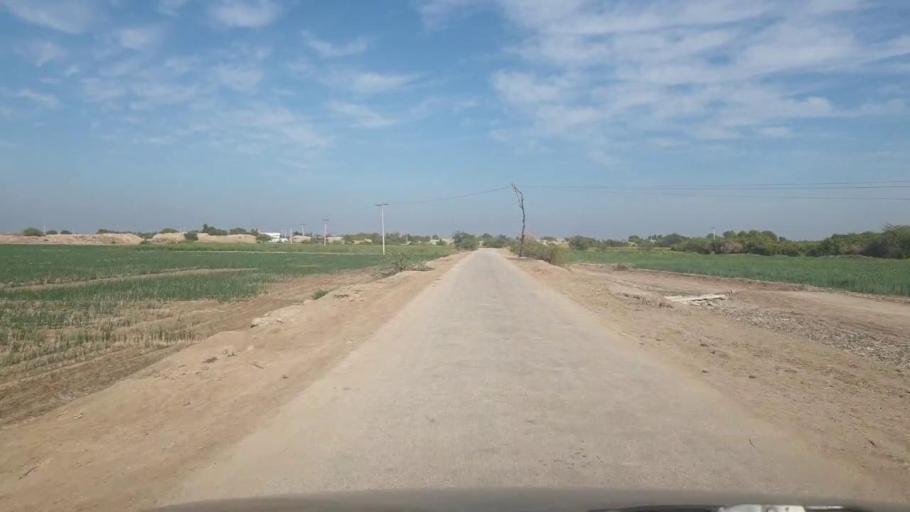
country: PK
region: Sindh
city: Pithoro
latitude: 25.4410
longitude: 69.2093
